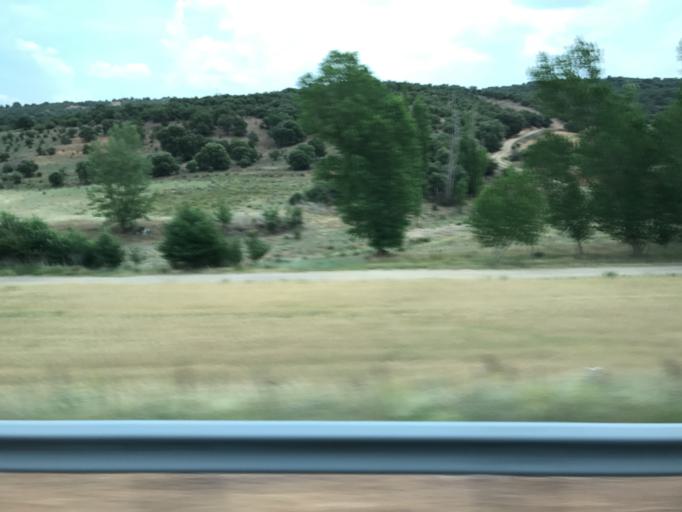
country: ES
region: Castille and Leon
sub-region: Provincia de Burgos
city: Pardilla
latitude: 41.5337
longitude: -3.7154
